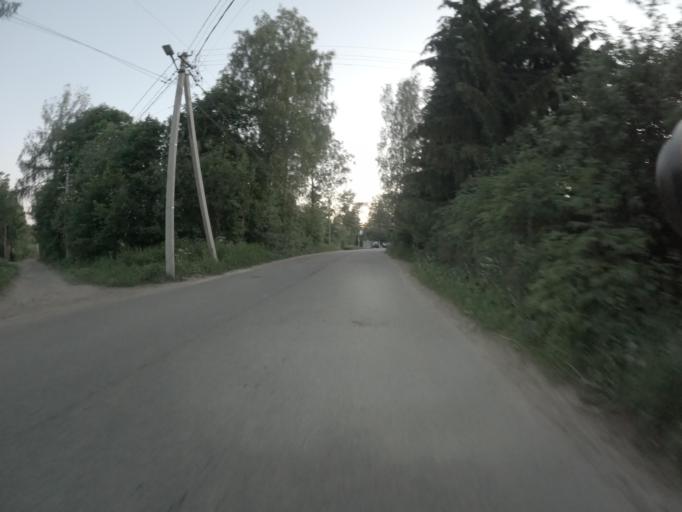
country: RU
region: Leningrad
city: Vsevolozhsk
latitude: 60.0119
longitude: 30.6083
